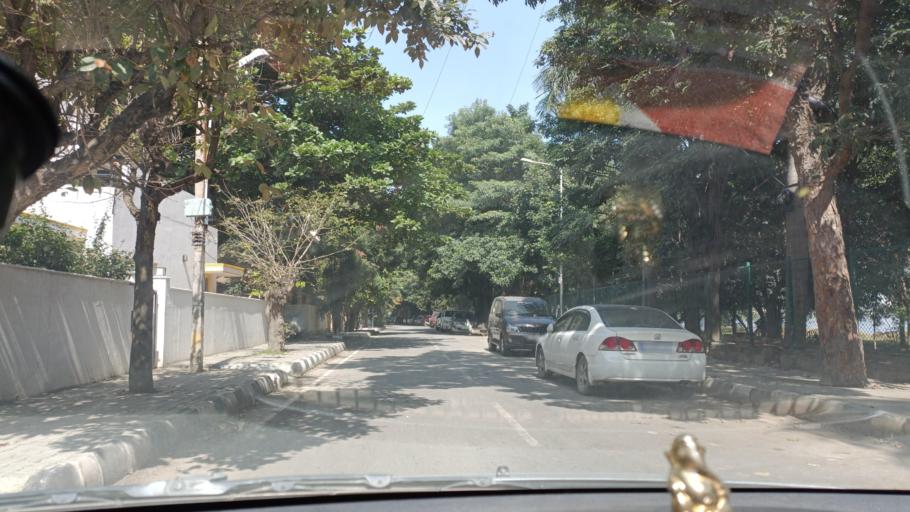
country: IN
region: Karnataka
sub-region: Bangalore Urban
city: Bangalore
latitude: 12.9088
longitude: 77.6149
